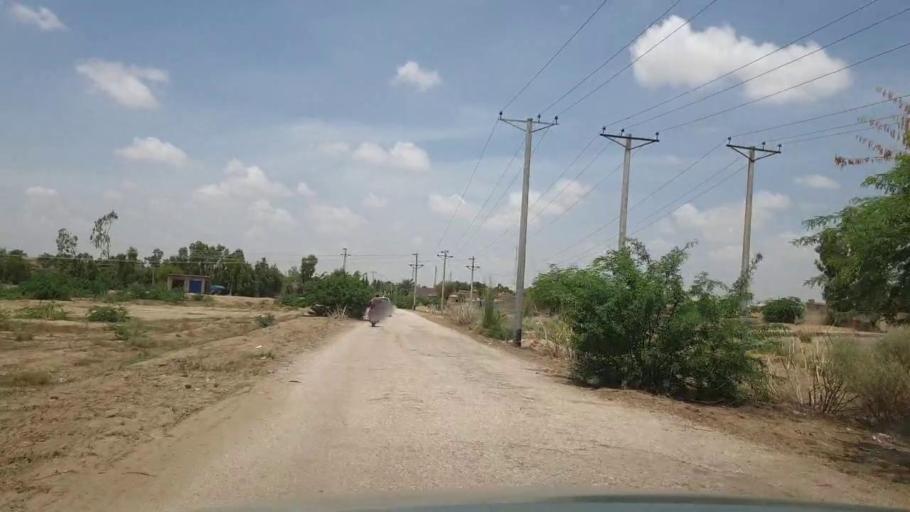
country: PK
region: Sindh
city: Kot Diji
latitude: 27.1584
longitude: 68.9685
